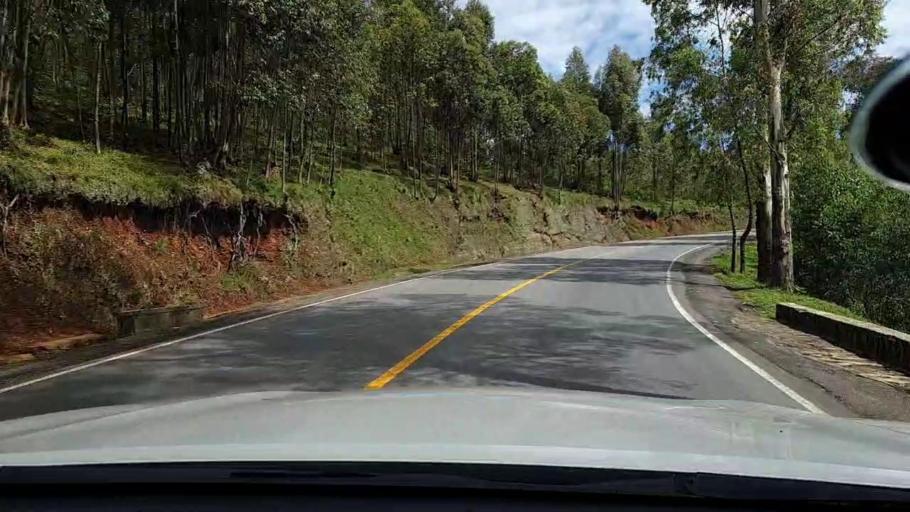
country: RW
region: Kigali
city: Kigali
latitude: -1.8262
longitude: 29.9473
